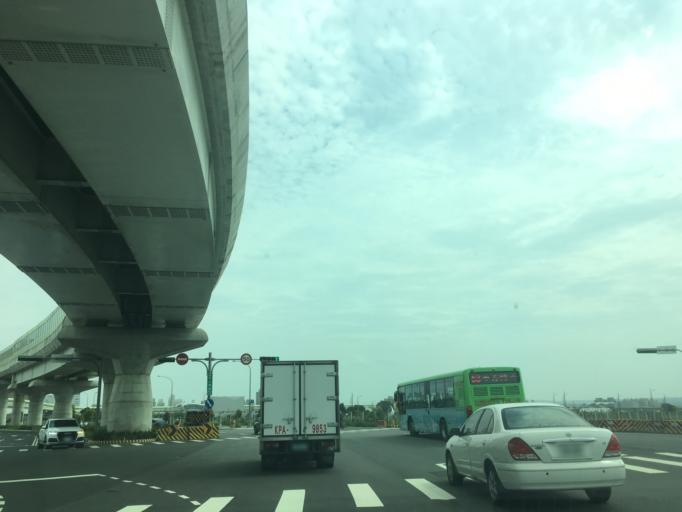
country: TW
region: Taiwan
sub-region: Taichung City
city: Taichung
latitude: 24.1264
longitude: 120.6462
